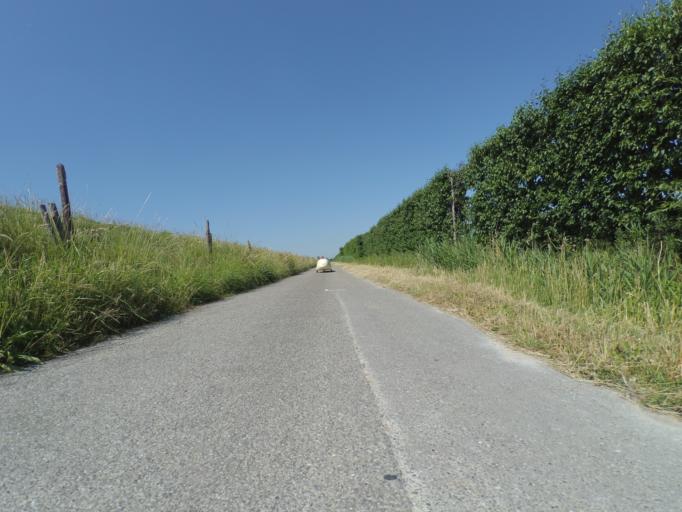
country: NL
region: Zeeland
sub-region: Gemeente Reimerswaal
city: Yerseke
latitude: 51.4421
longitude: 4.0934
